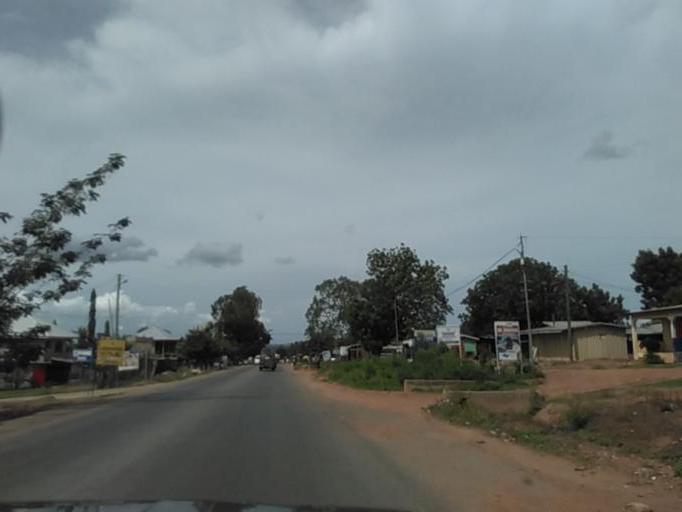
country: GH
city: Akropong
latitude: 6.2015
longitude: 0.0786
